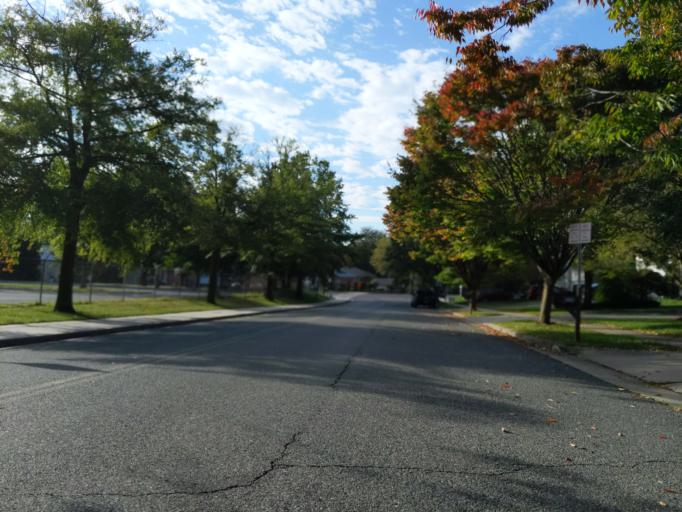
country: US
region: Maryland
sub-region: Montgomery County
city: Forest Glen
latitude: 39.0164
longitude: -77.0476
